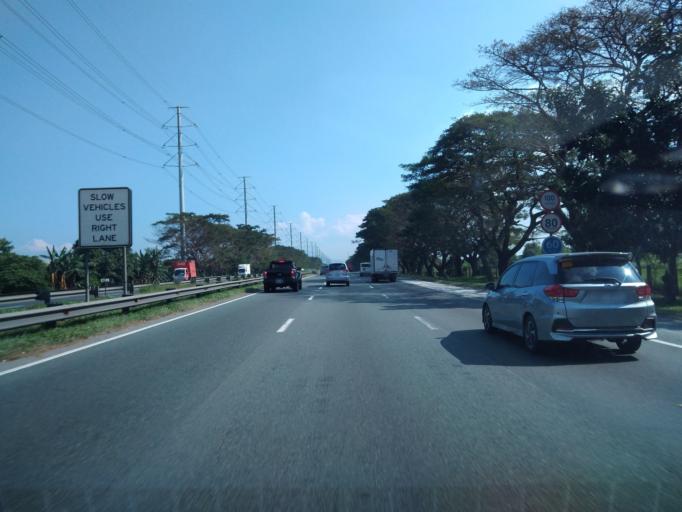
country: PH
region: Calabarzon
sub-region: Province of Laguna
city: Pulong Santa Cruz
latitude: 14.2670
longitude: 121.0976
